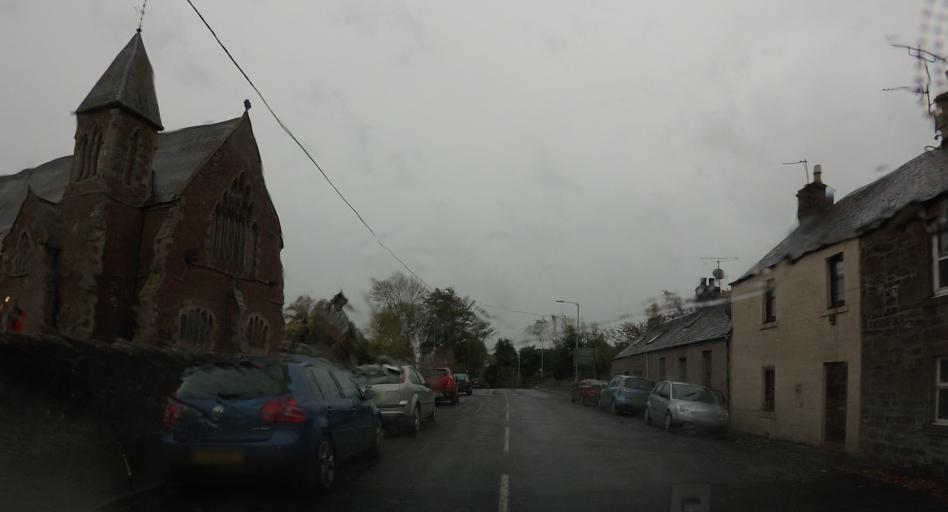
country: GB
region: Scotland
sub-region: Perth and Kinross
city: Coupar Angus
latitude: 56.5438
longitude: -3.2655
